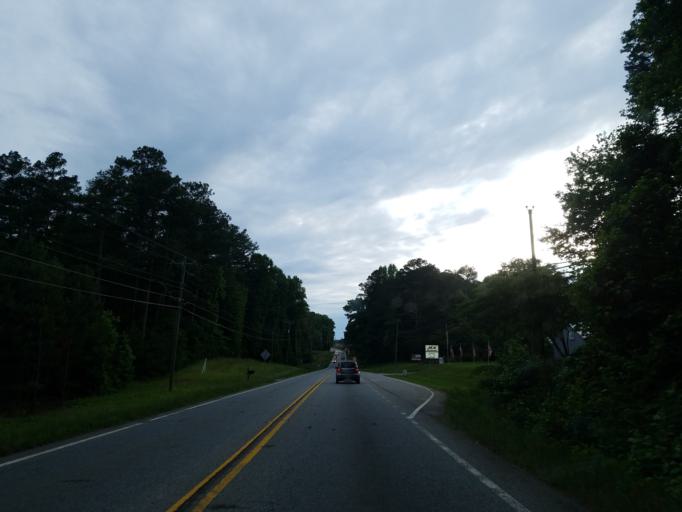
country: US
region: Georgia
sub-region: Forsyth County
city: Cumming
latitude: 34.2327
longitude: -84.1689
